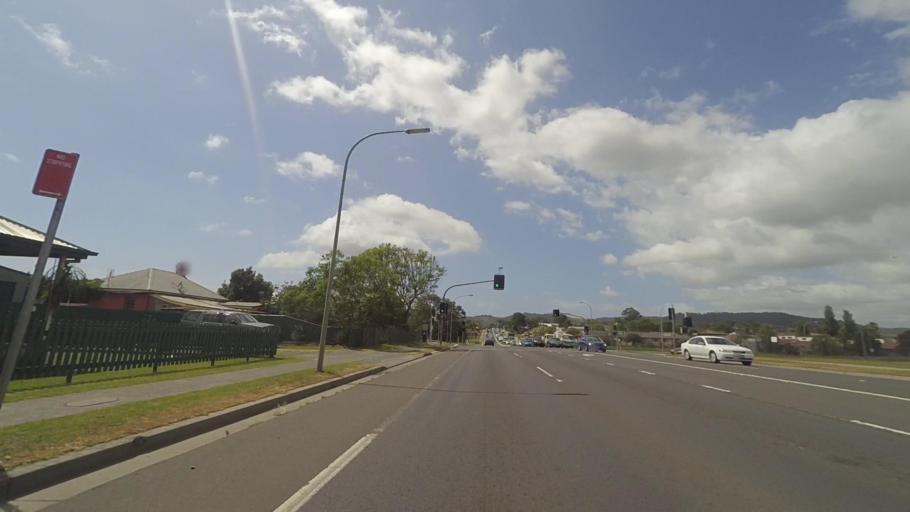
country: AU
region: New South Wales
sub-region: Shellharbour
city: Albion Park Rail
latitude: -34.5627
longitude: 150.7976
